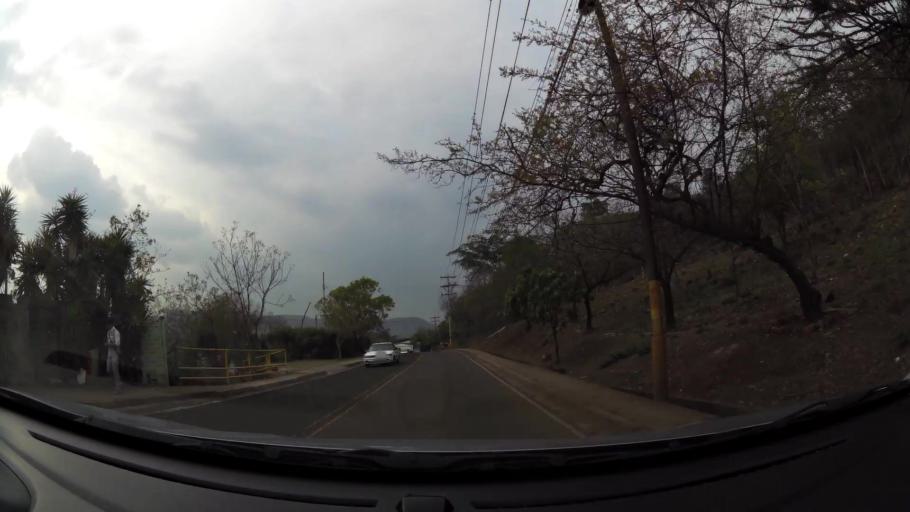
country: HN
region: Francisco Morazan
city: Tegucigalpa
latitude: 14.0919
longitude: -87.2036
